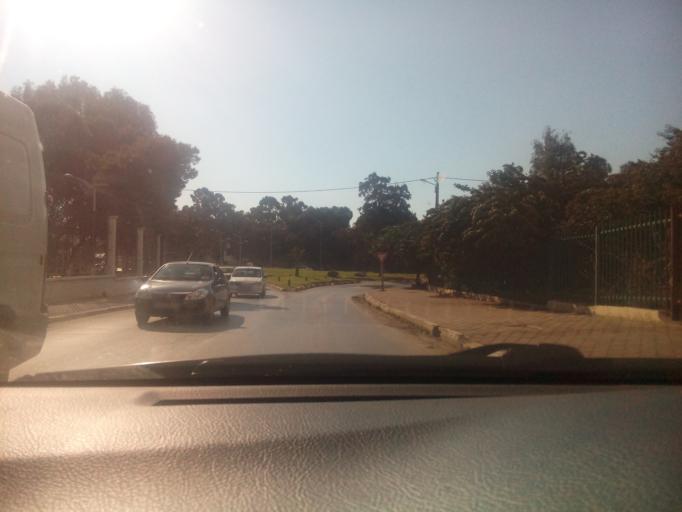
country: DZ
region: Oran
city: Oran
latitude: 35.7021
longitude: -0.6078
